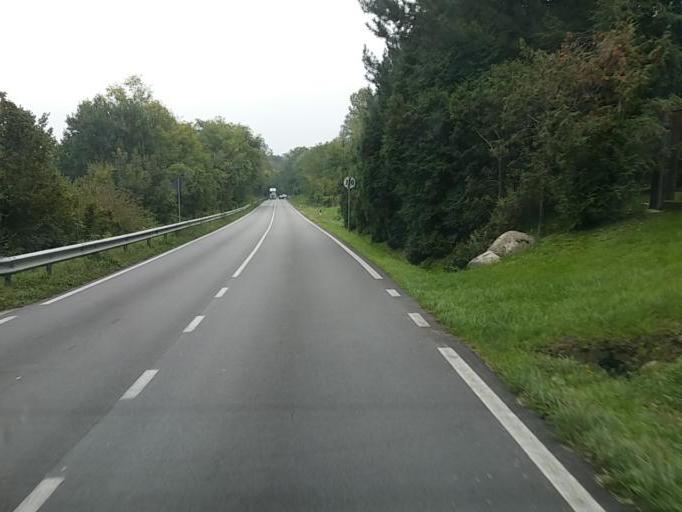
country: IT
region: Lombardy
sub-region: Provincia di Varese
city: Galliate Lombardo
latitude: 45.7901
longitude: 8.7695
